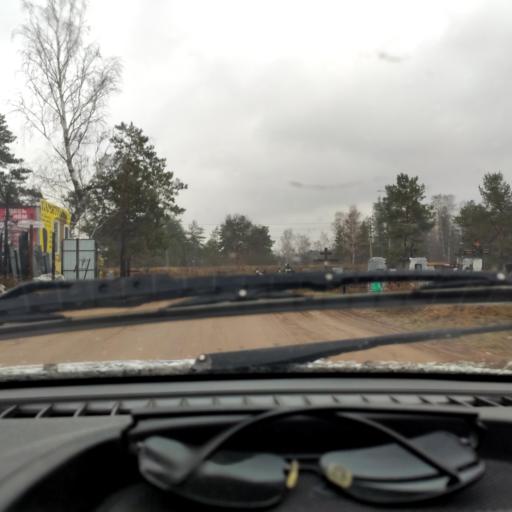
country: RU
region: Samara
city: Zhigulevsk
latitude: 53.5332
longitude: 49.5553
